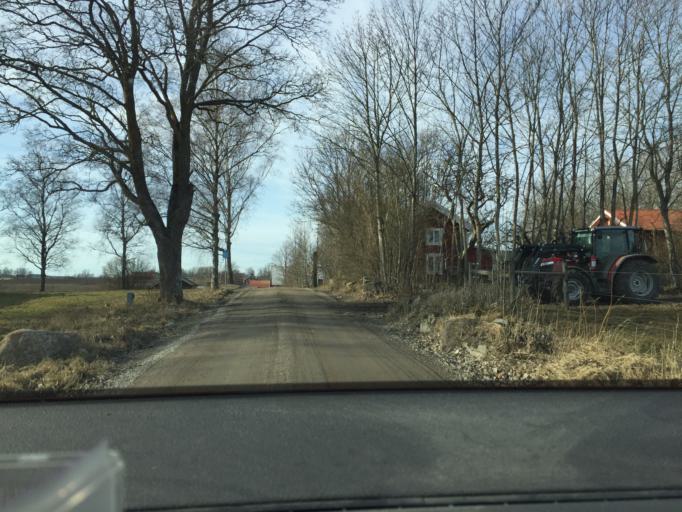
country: SE
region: OErebro
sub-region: Hallsbergs Kommun
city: Skollersta
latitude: 59.1354
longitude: 15.4222
